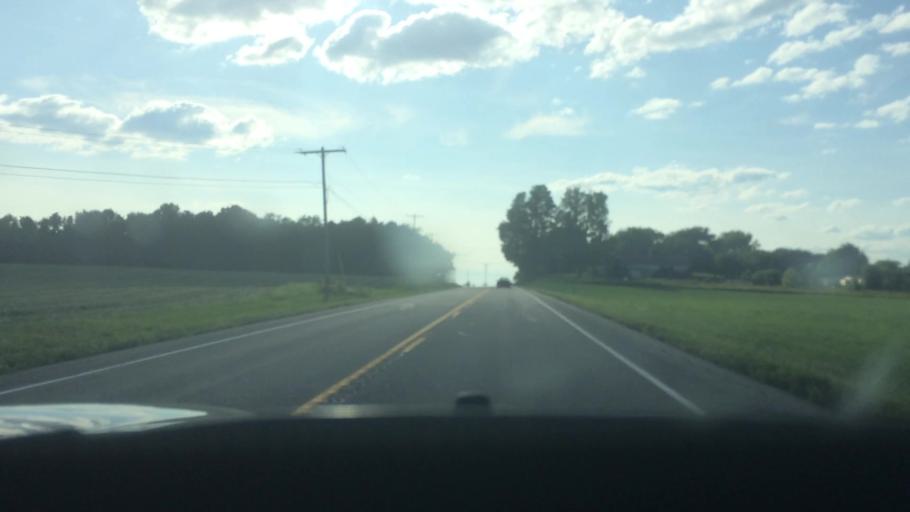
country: US
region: New York
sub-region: St. Lawrence County
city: Potsdam
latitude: 44.6897
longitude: -74.7426
